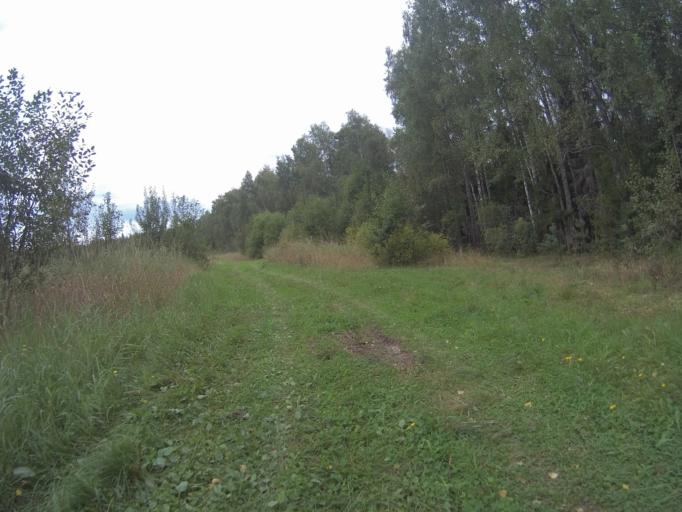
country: RU
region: Vladimir
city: Kommunar
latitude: 56.0329
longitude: 40.4939
